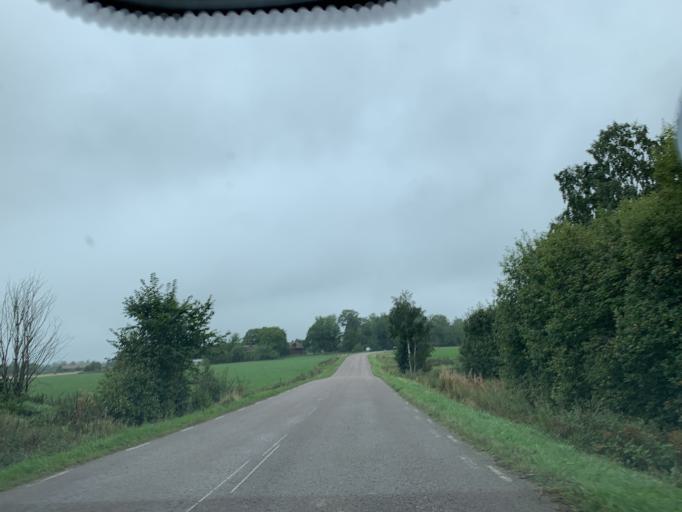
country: SE
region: Soedermanland
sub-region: Eskilstuna Kommun
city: Kvicksund
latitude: 59.5488
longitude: 16.4076
